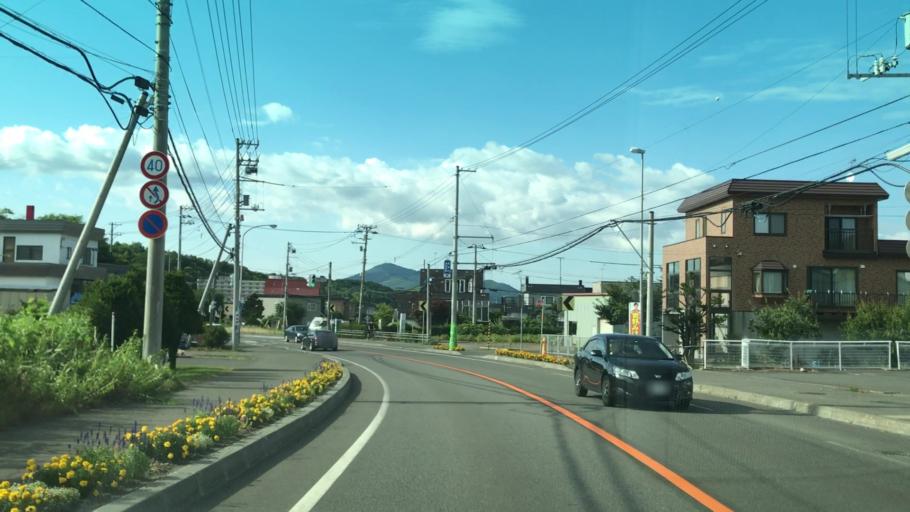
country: JP
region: Hokkaido
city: Sapporo
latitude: 42.9506
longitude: 141.3466
